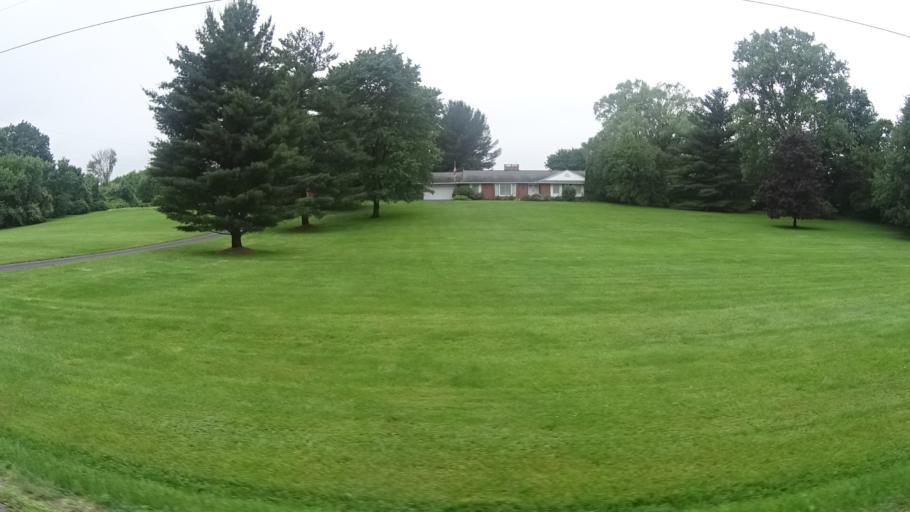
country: US
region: Ohio
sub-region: Erie County
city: Huron
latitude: 41.3488
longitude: -82.5765
